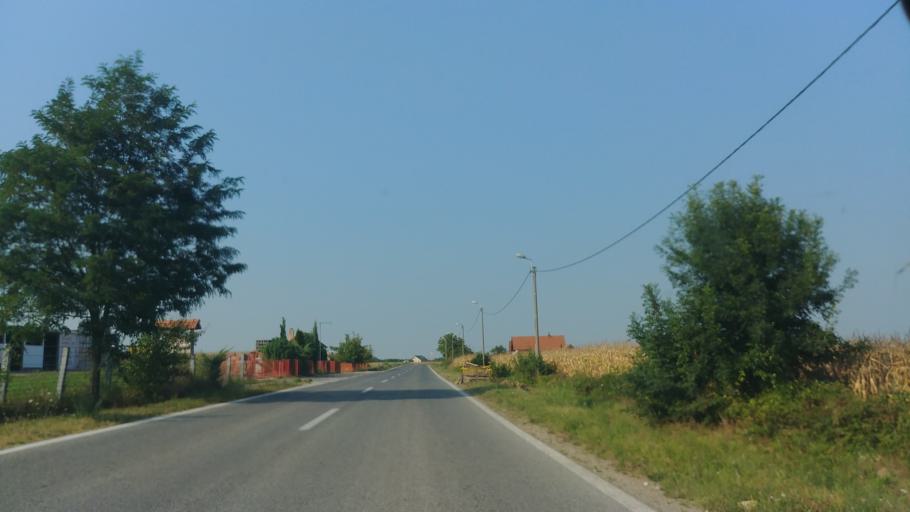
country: BA
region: Brcko
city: Brcko
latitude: 44.7765
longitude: 18.8099
